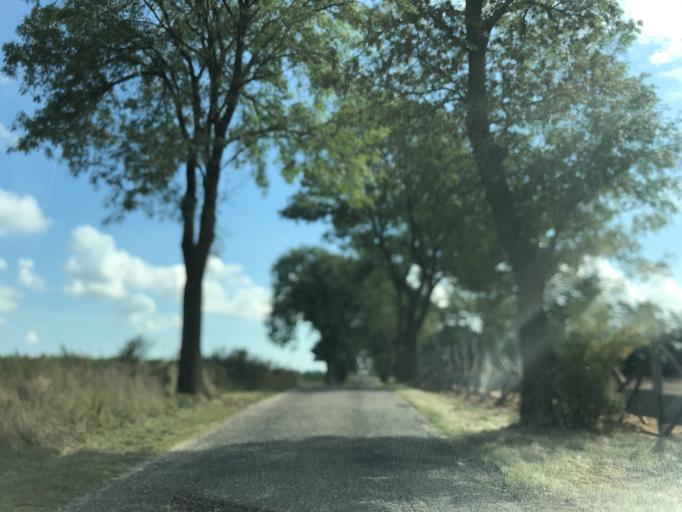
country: PL
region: Kujawsko-Pomorskie
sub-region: Powiat brodnicki
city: Brzozie
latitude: 53.3562
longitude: 19.6259
